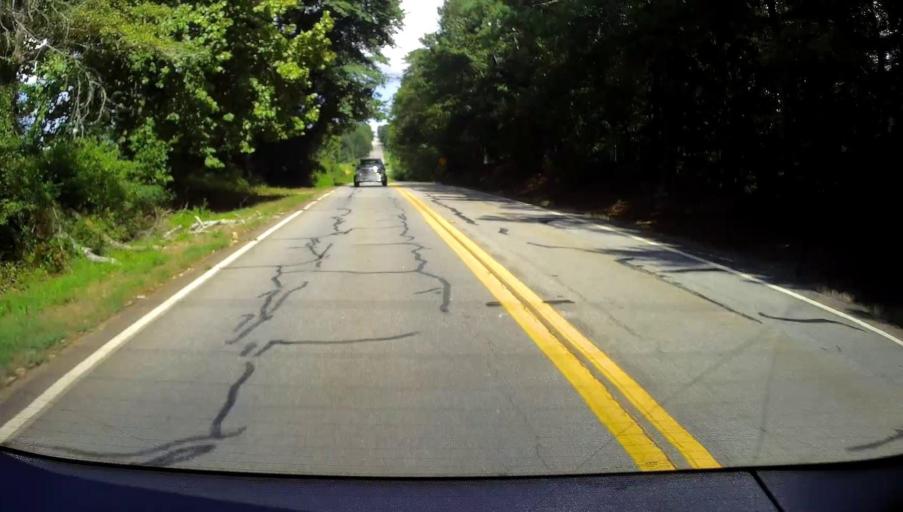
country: US
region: Georgia
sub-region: Upson County
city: Thomaston
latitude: 32.9217
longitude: -84.2161
